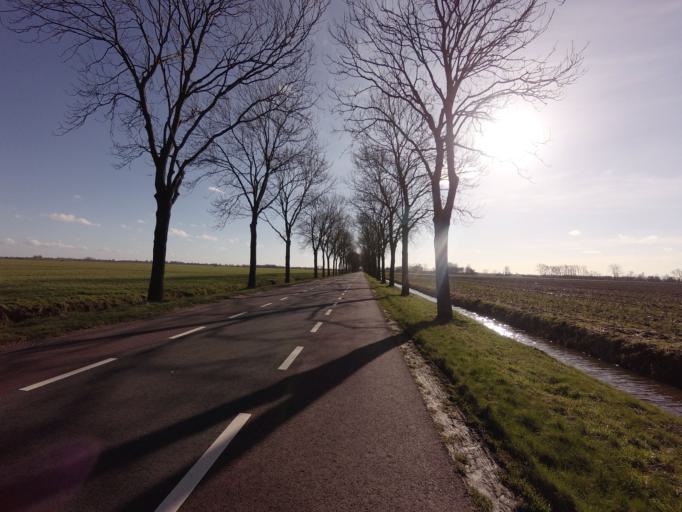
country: NL
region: Utrecht
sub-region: Gemeente Montfoort
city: Montfoort
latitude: 52.0714
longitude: 4.9602
